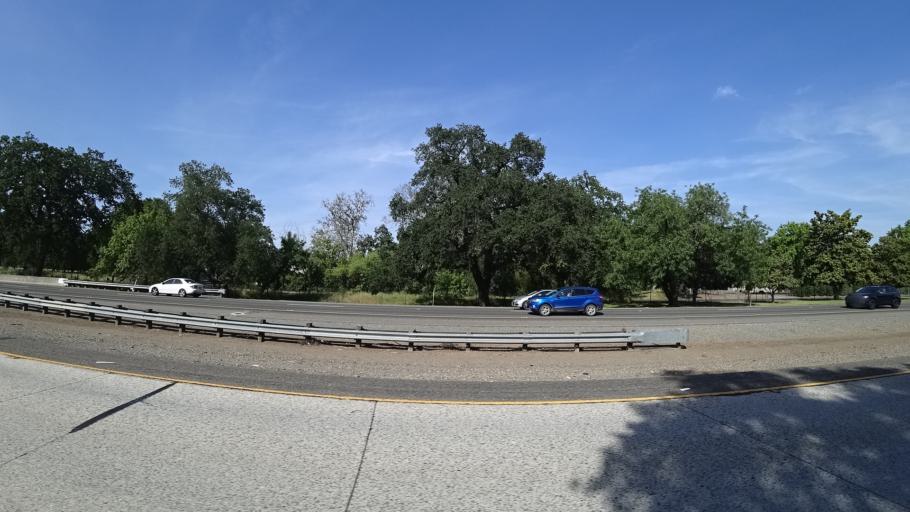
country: US
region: California
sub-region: Butte County
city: Chico
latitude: 39.7081
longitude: -121.7938
